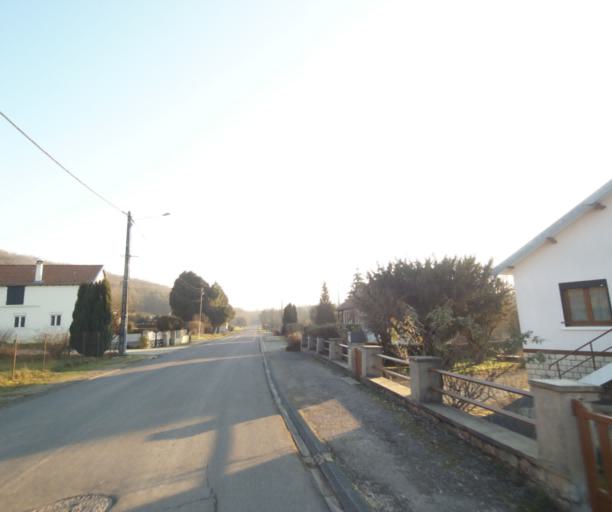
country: FR
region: Champagne-Ardenne
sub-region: Departement de la Haute-Marne
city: Chevillon
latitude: 48.5375
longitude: 5.1060
